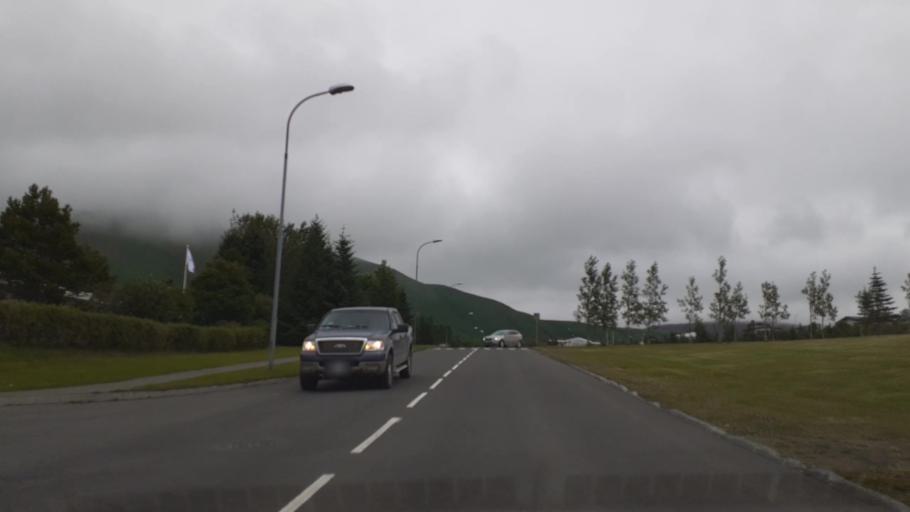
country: IS
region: Northeast
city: Husavik
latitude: 66.0372
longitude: -17.3367
